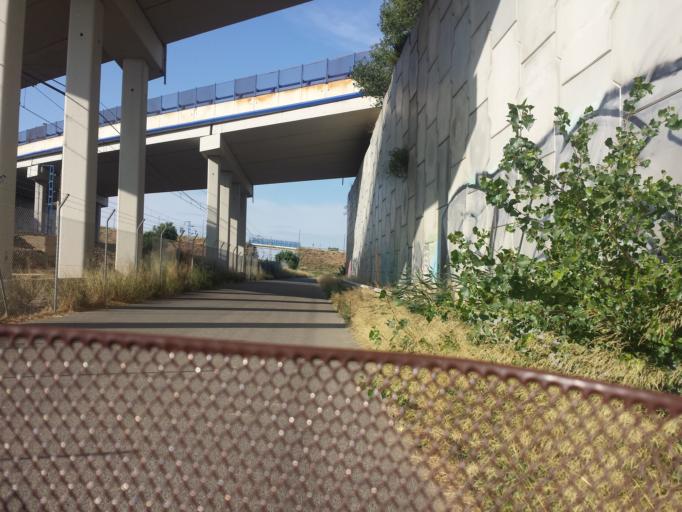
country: ES
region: Aragon
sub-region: Provincia de Zaragoza
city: Zaragoza
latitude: 41.7105
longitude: -0.8485
